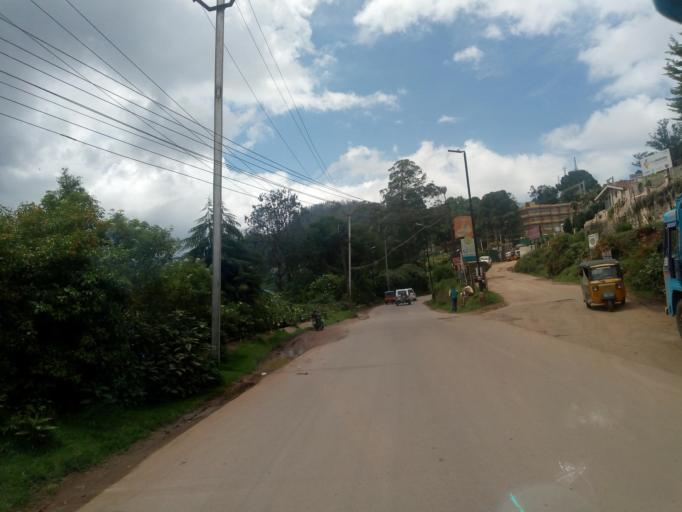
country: IN
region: Tamil Nadu
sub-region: Nilgiri
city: Ooty
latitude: 11.4022
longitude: 76.6969
